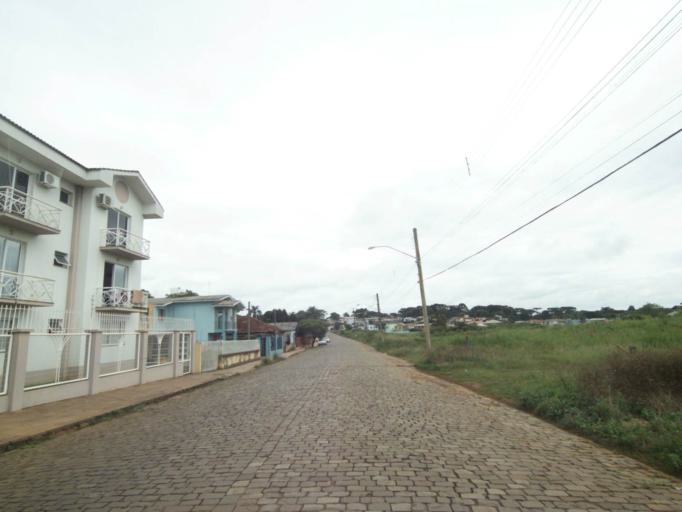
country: BR
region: Rio Grande do Sul
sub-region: Lagoa Vermelha
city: Lagoa Vermelha
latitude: -28.2145
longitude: -51.5221
